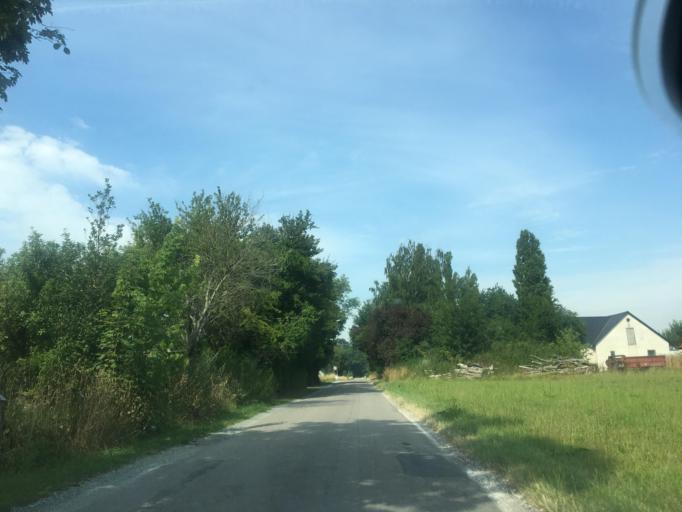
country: DK
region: Zealand
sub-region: Vordingborg Kommune
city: Praesto
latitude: 55.1819
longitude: 12.0877
